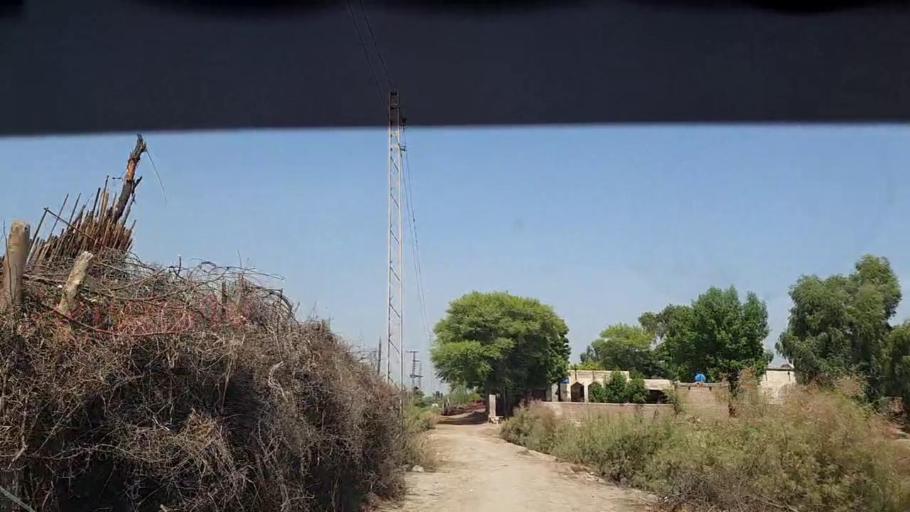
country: PK
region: Sindh
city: Ghauspur
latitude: 28.1646
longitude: 69.1433
